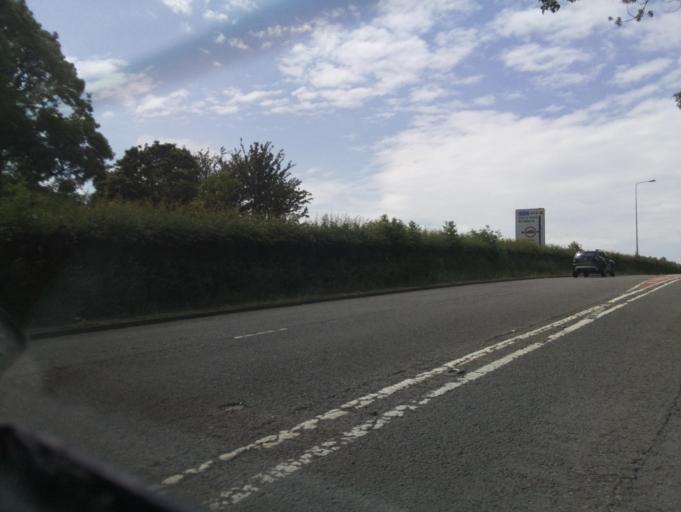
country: GB
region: Wales
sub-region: Vale of Glamorgan
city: Penllyn
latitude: 51.4701
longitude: -3.4840
